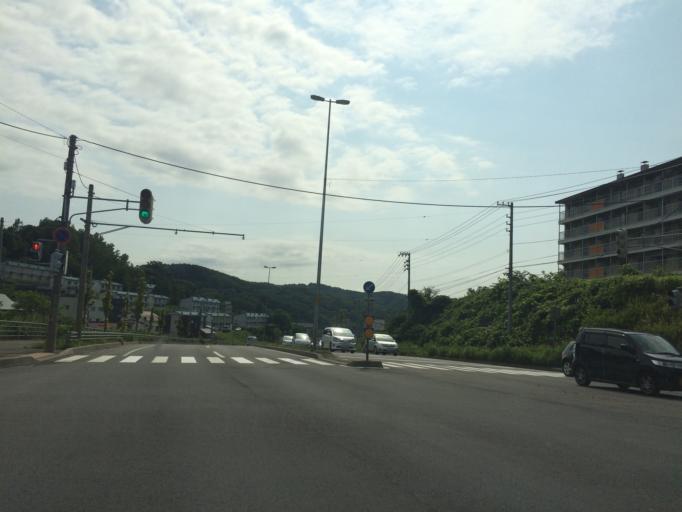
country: JP
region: Hokkaido
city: Otaru
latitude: 43.2113
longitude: 140.9351
